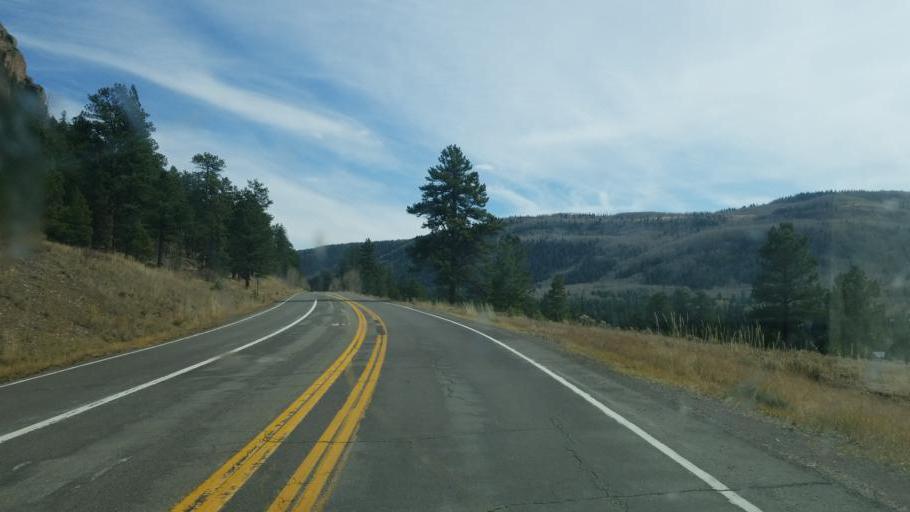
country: US
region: Colorado
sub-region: Conejos County
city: Conejos
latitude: 37.0824
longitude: -106.2993
